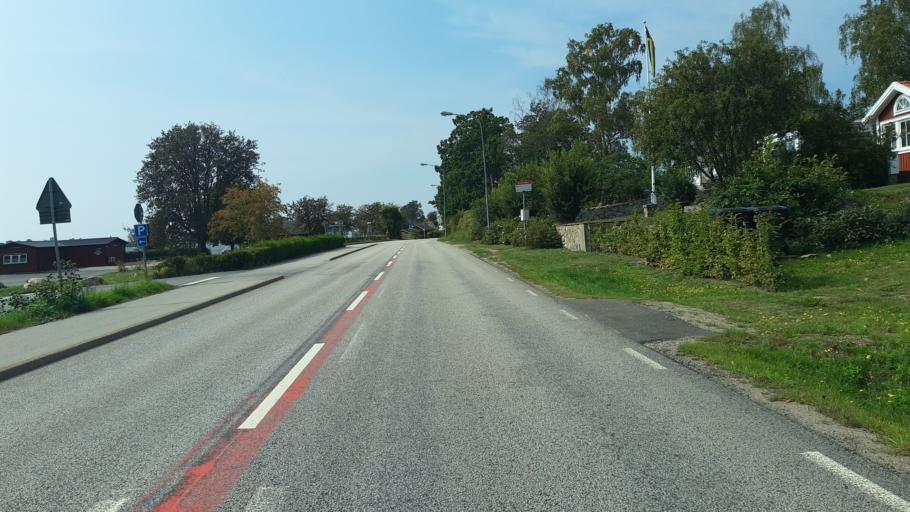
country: SE
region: Blekinge
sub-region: Ronneby Kommun
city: Ronneby
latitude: 56.1730
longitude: 15.2820
